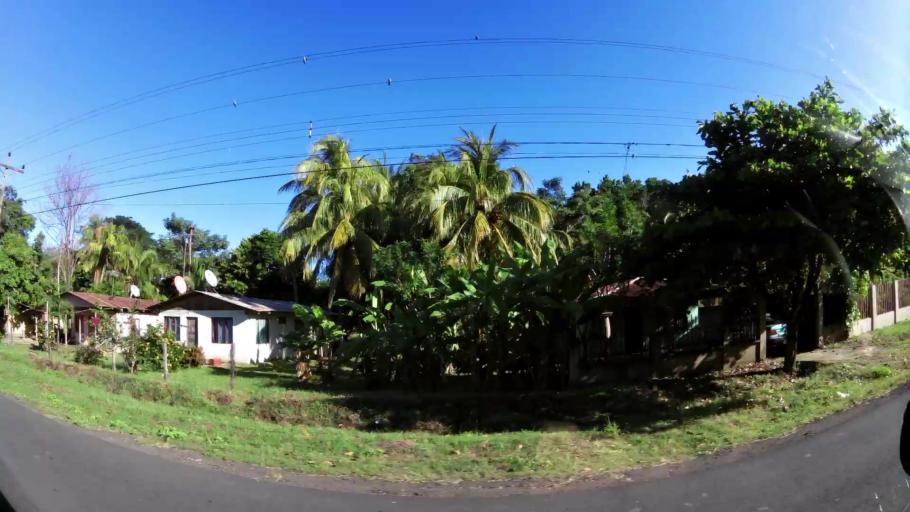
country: CR
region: Guanacaste
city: Sardinal
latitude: 10.4905
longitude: -85.6294
